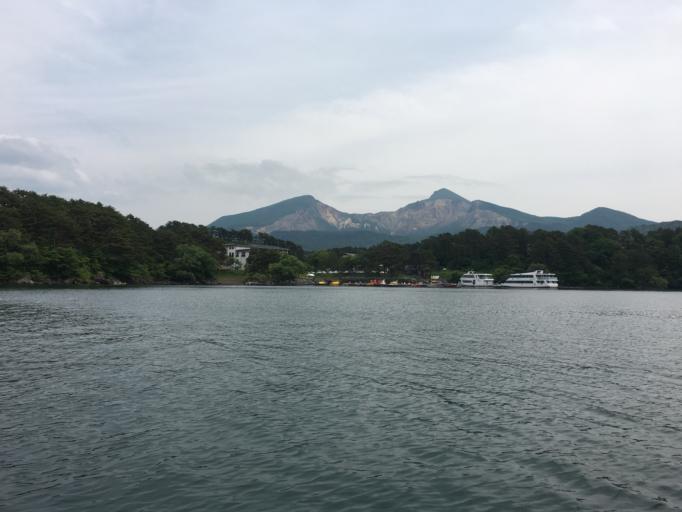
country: JP
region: Fukushima
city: Inawashiro
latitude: 37.6556
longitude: 140.0631
